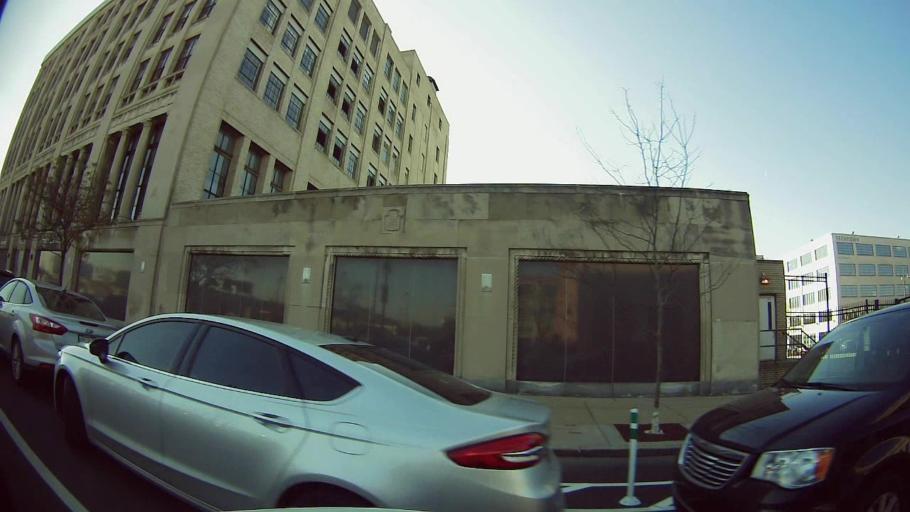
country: US
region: Michigan
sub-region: Wayne County
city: Hamtramck
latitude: 42.3647
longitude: -83.0716
